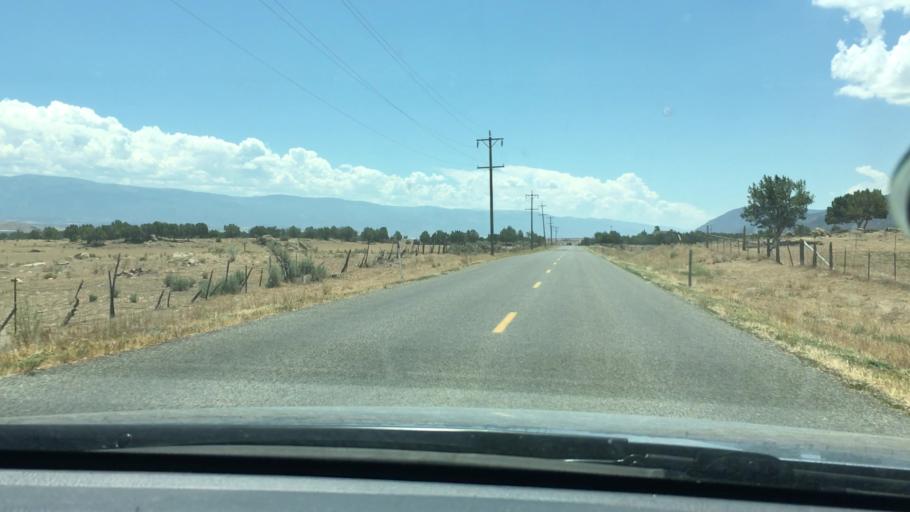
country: US
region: Utah
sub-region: Sanpete County
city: Fountain Green
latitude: 39.5951
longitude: -111.6430
